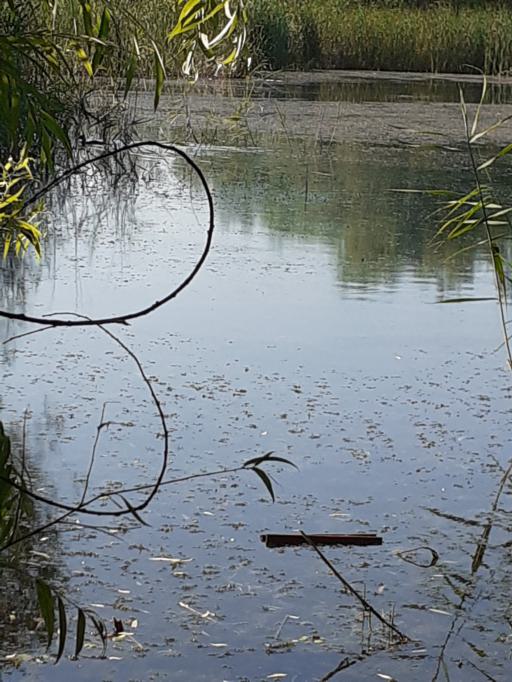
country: RO
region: Ilfov
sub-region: Comuna Popesti-Leordeni
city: Popesti-Leordeni
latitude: 44.4017
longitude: 26.1339
